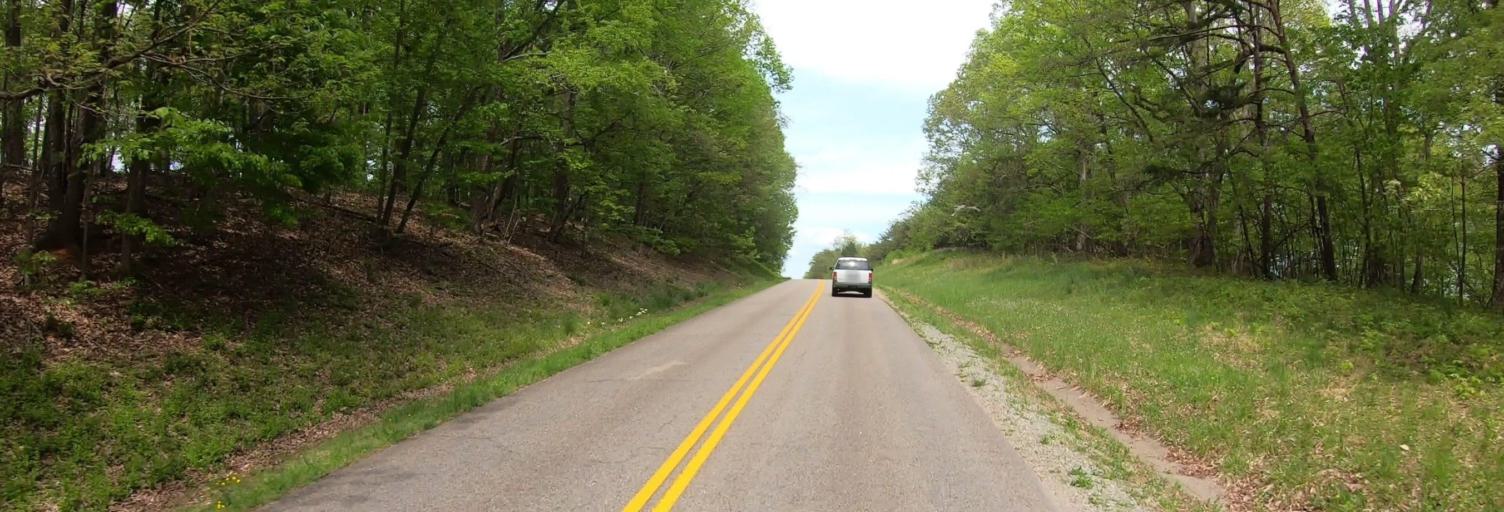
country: US
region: Virginia
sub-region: City of Roanoke
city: Cedar Bluff
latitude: 37.2284
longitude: -79.9078
